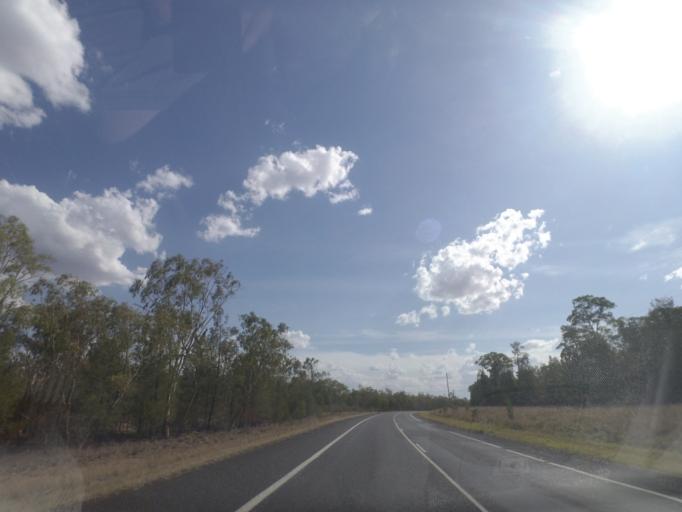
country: AU
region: New South Wales
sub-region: Moree Plains
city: Boggabilla
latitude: -28.5420
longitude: 150.8848
